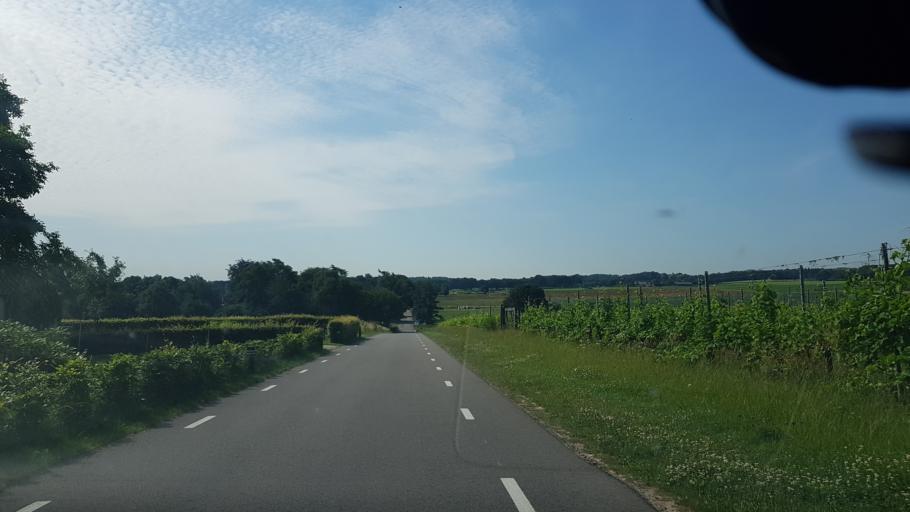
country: NL
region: Gelderland
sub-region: Gemeente Groesbeek
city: Bredeweg
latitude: 51.7612
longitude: 5.9339
